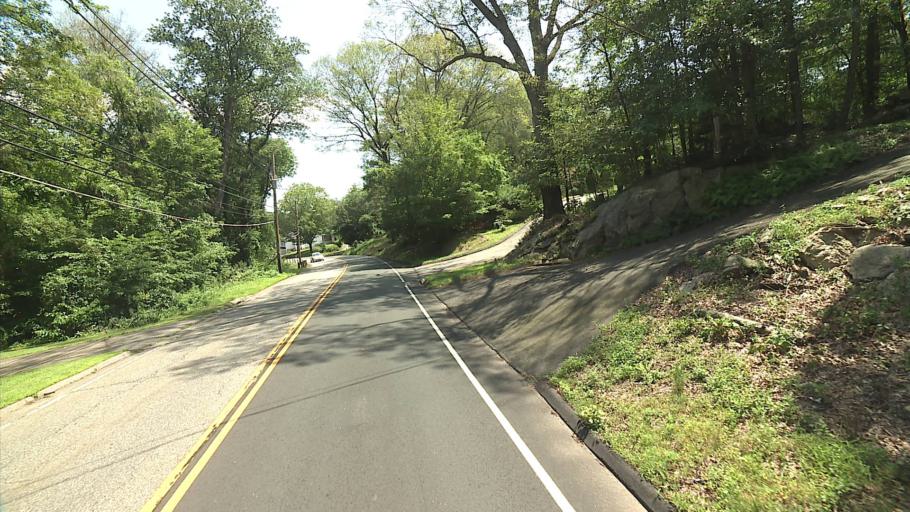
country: US
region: Connecticut
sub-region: Middlesex County
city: Essex Village
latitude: 41.3556
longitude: -72.4201
